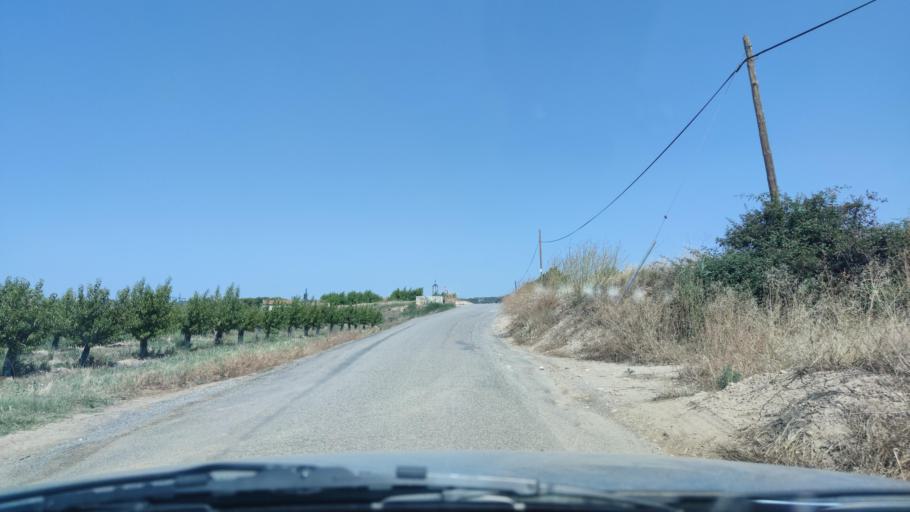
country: ES
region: Catalonia
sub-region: Provincia de Lleida
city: Alpicat
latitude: 41.6600
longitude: 0.5617
